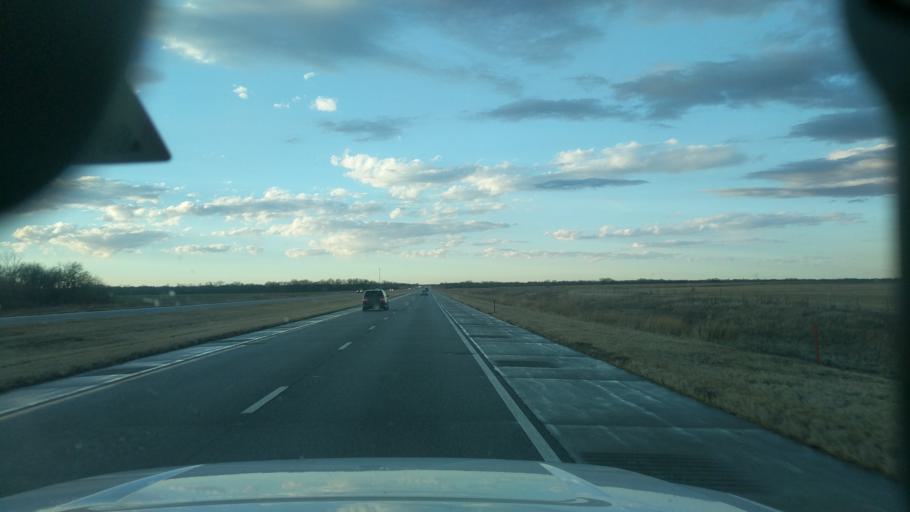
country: US
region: Kansas
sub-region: Harvey County
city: Hesston
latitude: 38.1774
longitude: -97.4518
